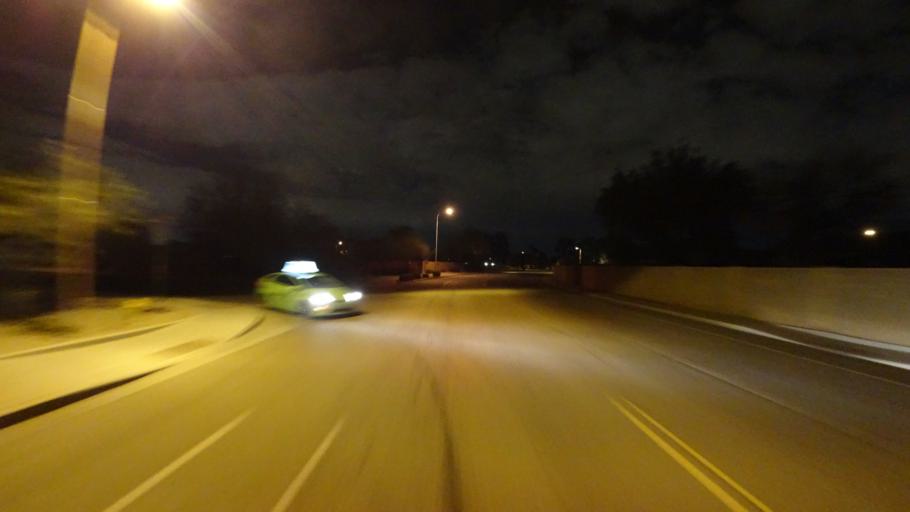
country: US
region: Arizona
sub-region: Maricopa County
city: San Carlos
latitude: 33.3296
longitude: -111.8505
